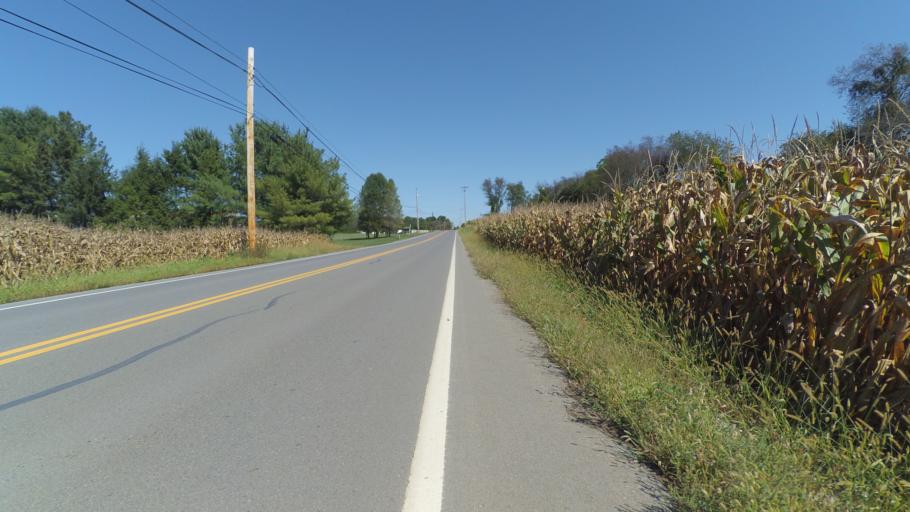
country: US
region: Pennsylvania
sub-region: Centre County
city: Park Forest Village
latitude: 40.7694
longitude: -77.9133
